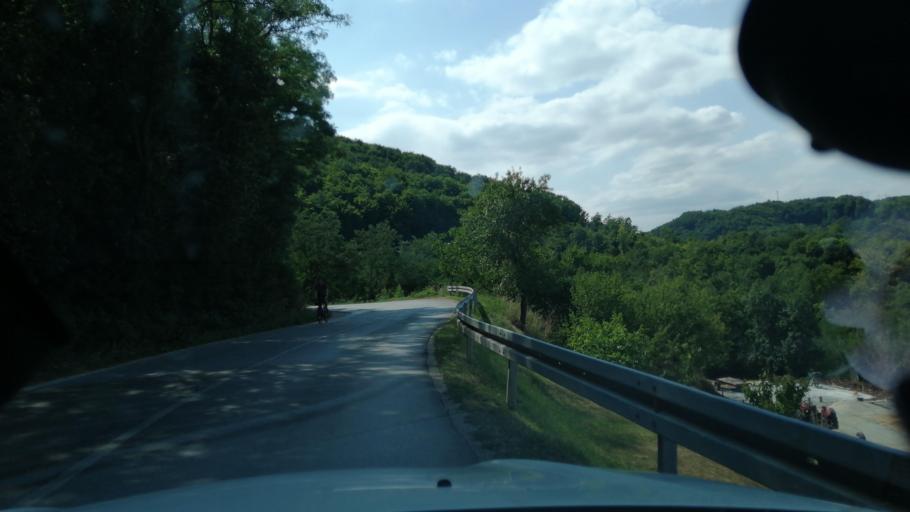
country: RS
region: Central Serbia
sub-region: Moravicki Okrug
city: Cacak
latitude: 43.8433
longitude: 20.2995
